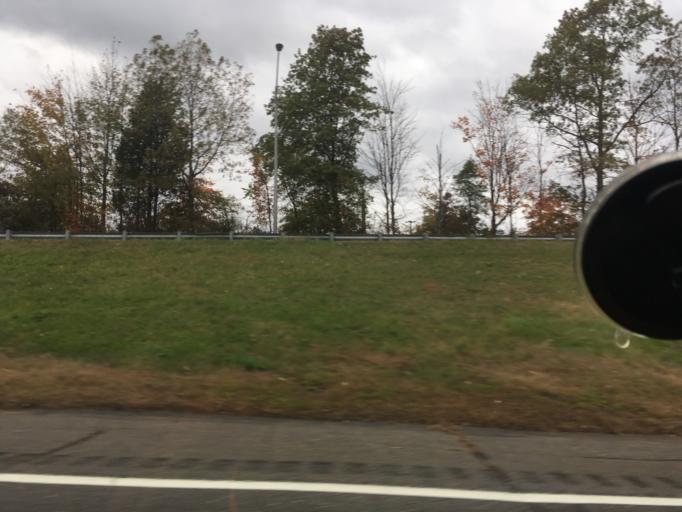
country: US
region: Massachusetts
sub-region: Bristol County
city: Seekonk
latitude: 41.7951
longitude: -71.3514
